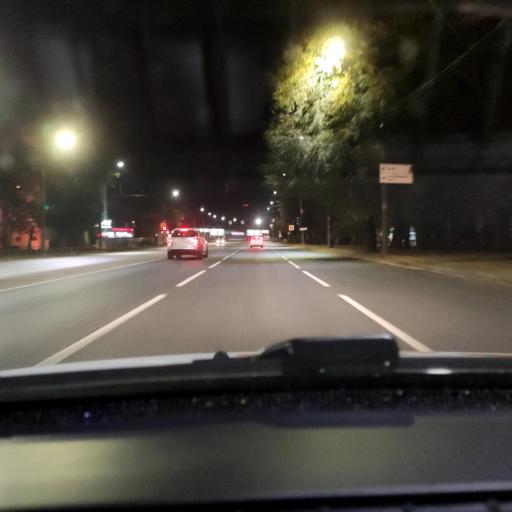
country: RU
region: Voronezj
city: Voronezh
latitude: 51.6785
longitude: 39.1740
